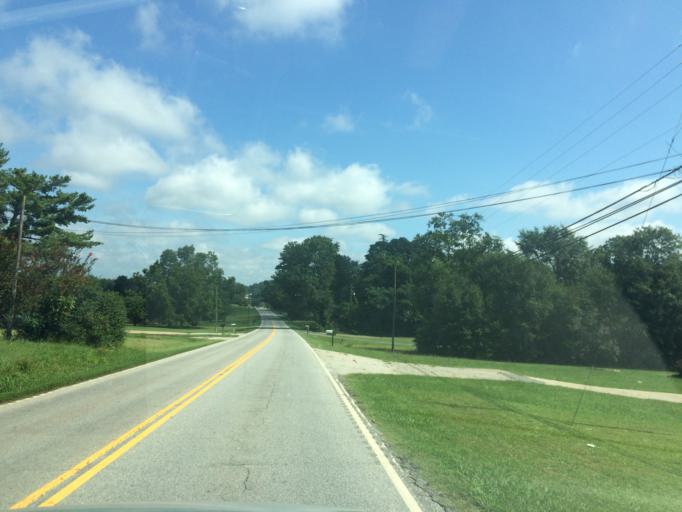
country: US
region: South Carolina
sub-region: Spartanburg County
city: Lyman
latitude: 34.9654
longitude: -82.1222
